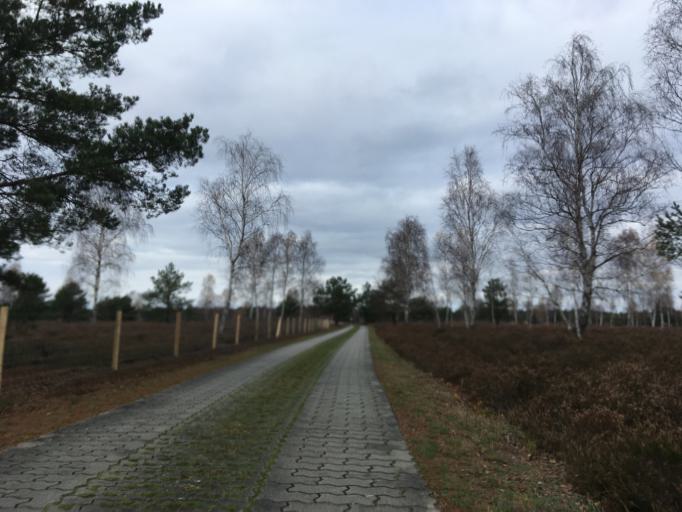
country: DE
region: Brandenburg
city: Tauer
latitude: 52.0096
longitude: 14.4948
